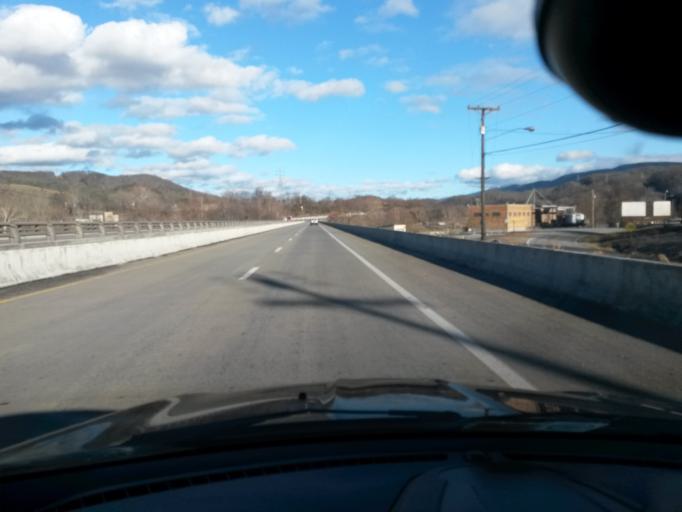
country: US
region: Virginia
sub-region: Giles County
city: Narrows
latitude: 37.3714
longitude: -80.8654
